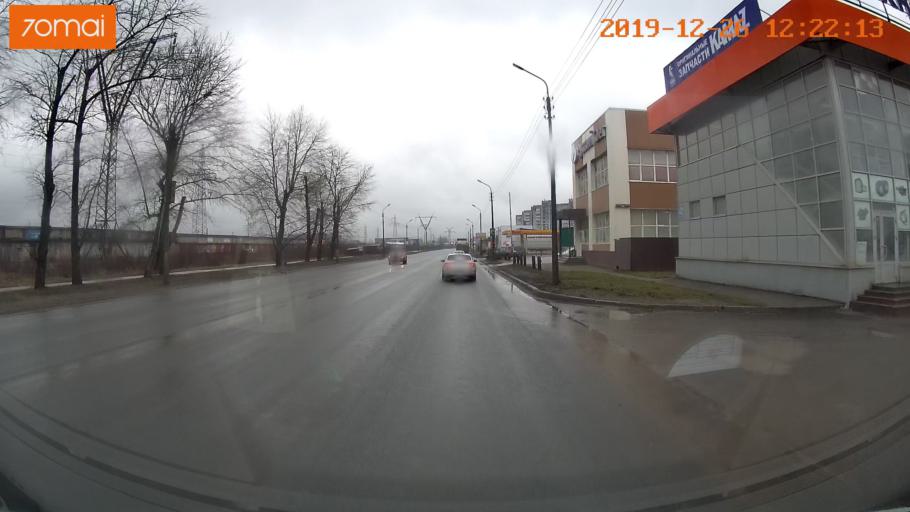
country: RU
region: Vologda
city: Tonshalovo
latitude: 59.1509
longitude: 37.9426
